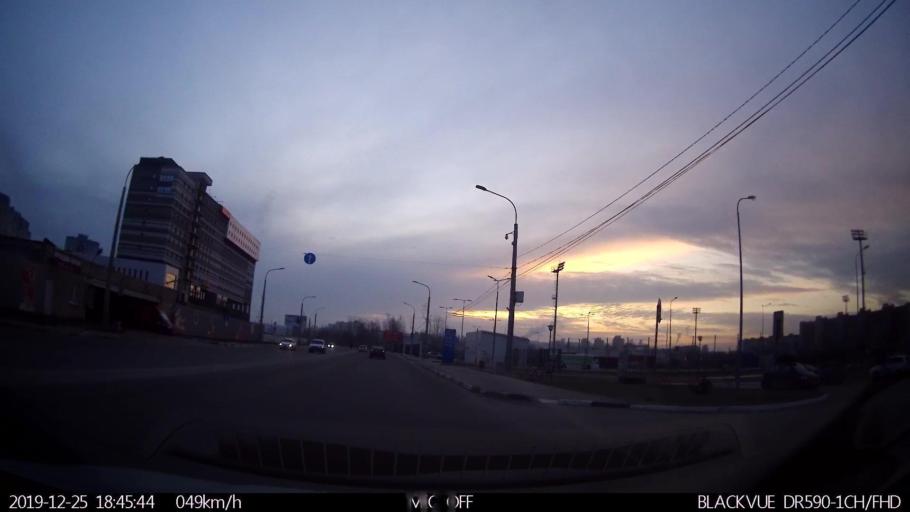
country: RU
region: Nizjnij Novgorod
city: Nizhniy Novgorod
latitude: 56.3393
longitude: 43.9451
